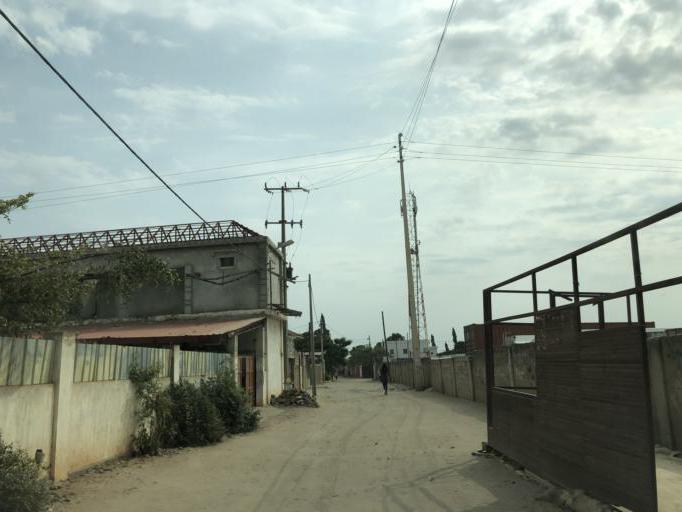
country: AO
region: Luanda
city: Luanda
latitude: -8.8943
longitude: 13.3552
